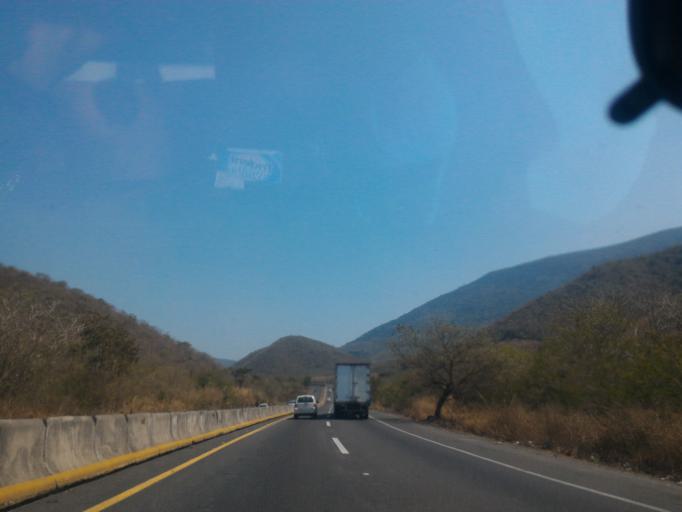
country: MX
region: Colima
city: Ixtlahuacan
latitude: 19.0229
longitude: -103.8125
